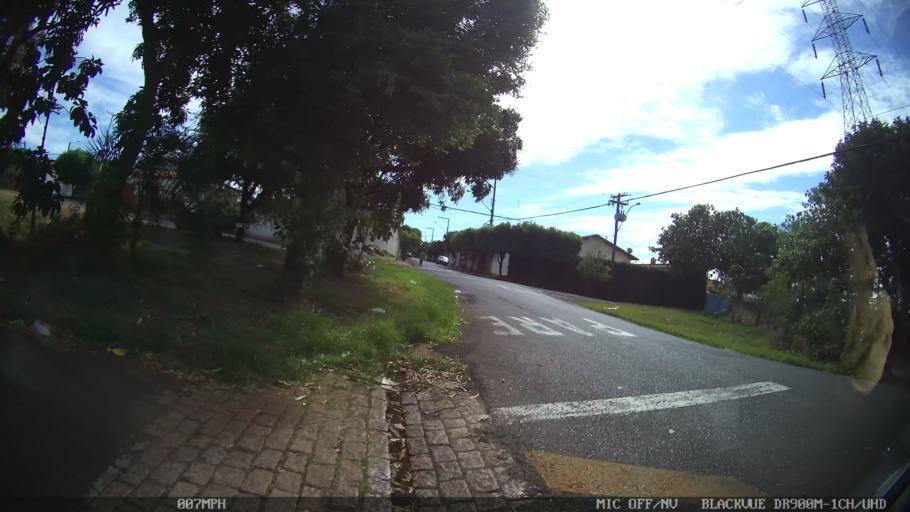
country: BR
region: Sao Paulo
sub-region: Sao Jose Do Rio Preto
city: Sao Jose do Rio Preto
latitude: -20.8334
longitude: -49.3496
